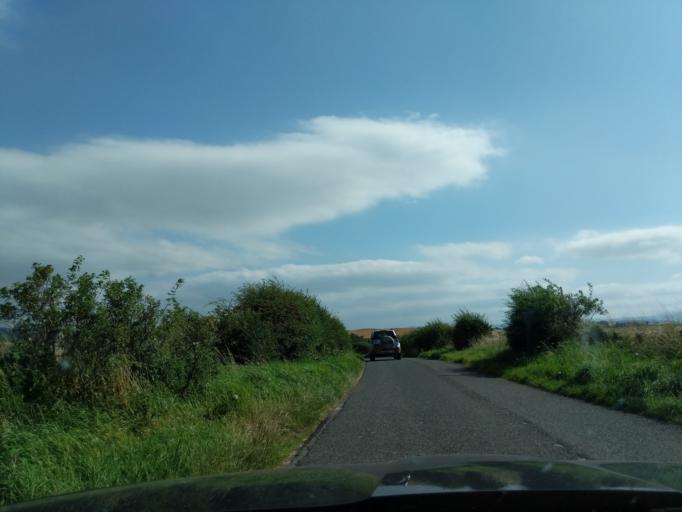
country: GB
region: England
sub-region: Northumberland
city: Ford
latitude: 55.6631
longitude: -2.1590
